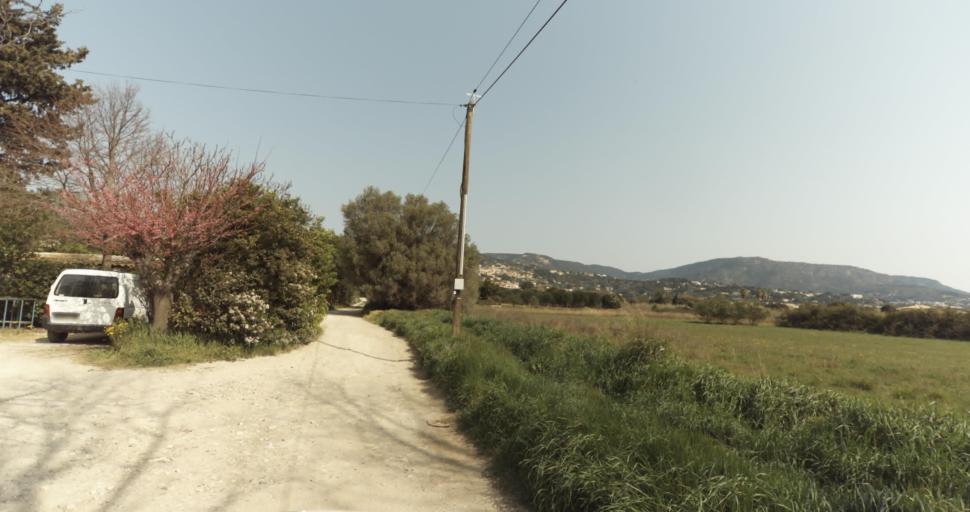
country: FR
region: Provence-Alpes-Cote d'Azur
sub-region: Departement du Var
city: Bormes-les-Mimosas
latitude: 43.1369
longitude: 6.3340
